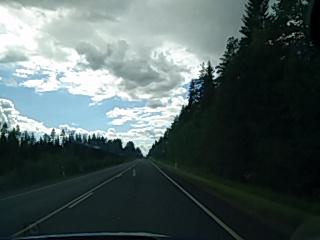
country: FI
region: Haeme
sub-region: Haemeenlinna
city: Renko
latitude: 60.8671
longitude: 24.1987
